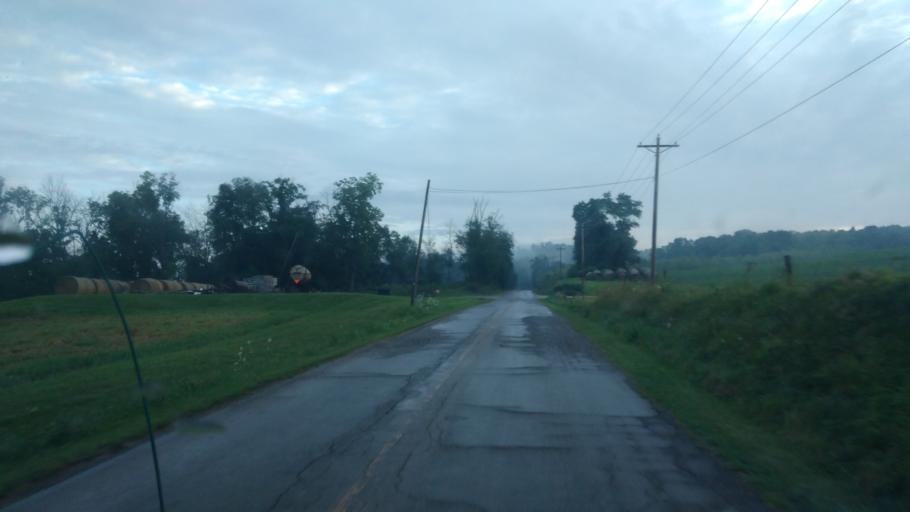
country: US
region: Ohio
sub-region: Guernsey County
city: Byesville
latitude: 39.9976
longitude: -81.3654
